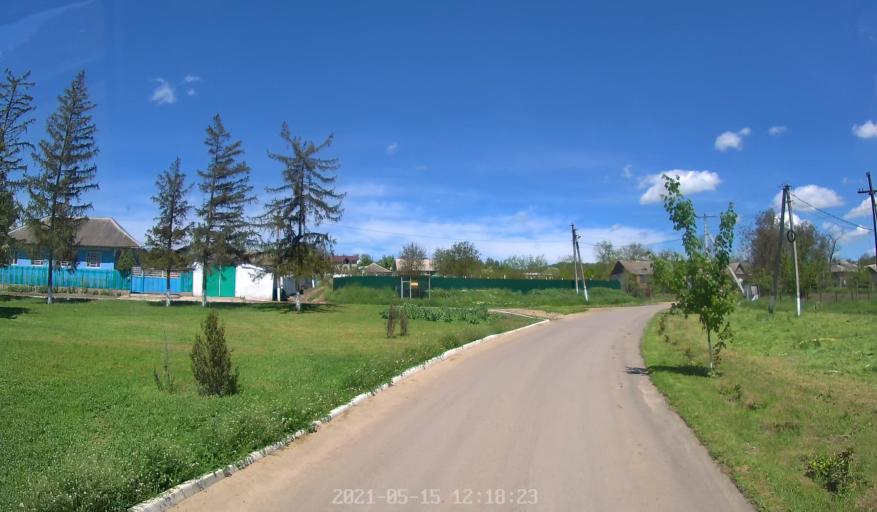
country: MD
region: Hincesti
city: Hincesti
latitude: 46.7973
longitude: 28.5411
